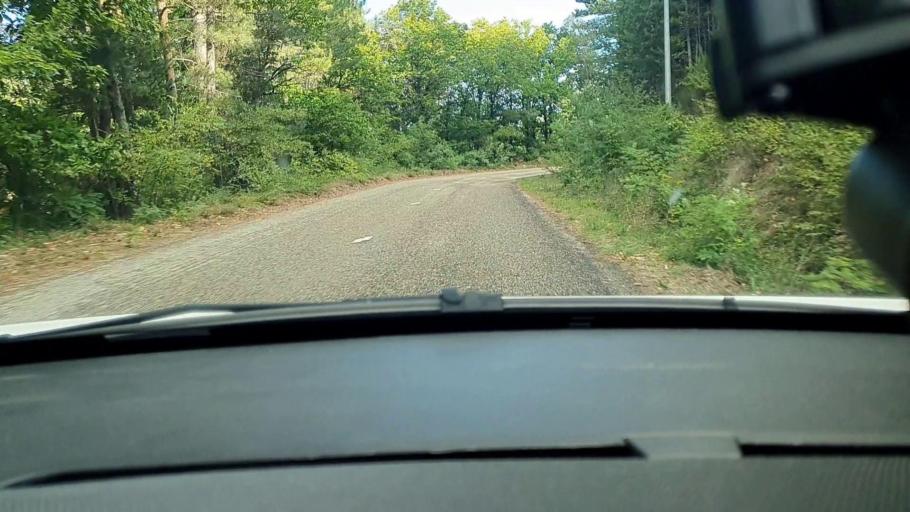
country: FR
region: Rhone-Alpes
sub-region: Departement de l'Ardeche
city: Les Vans
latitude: 44.4037
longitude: 4.0041
